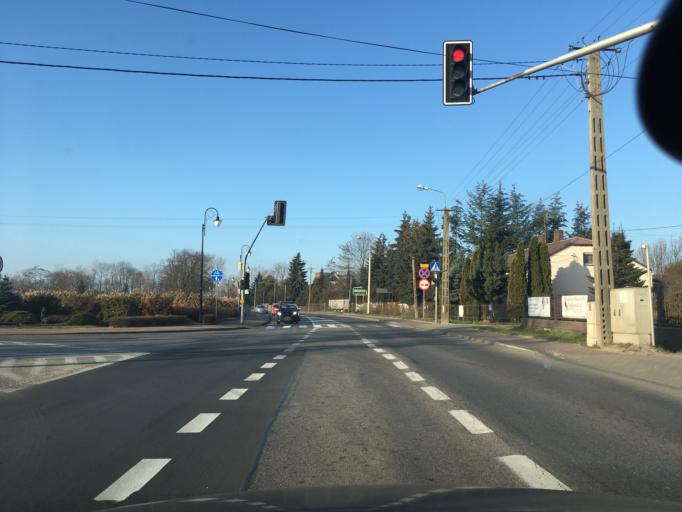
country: PL
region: Masovian Voivodeship
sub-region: Powiat piaseczynski
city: Lesznowola
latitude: 52.0876
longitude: 20.9421
